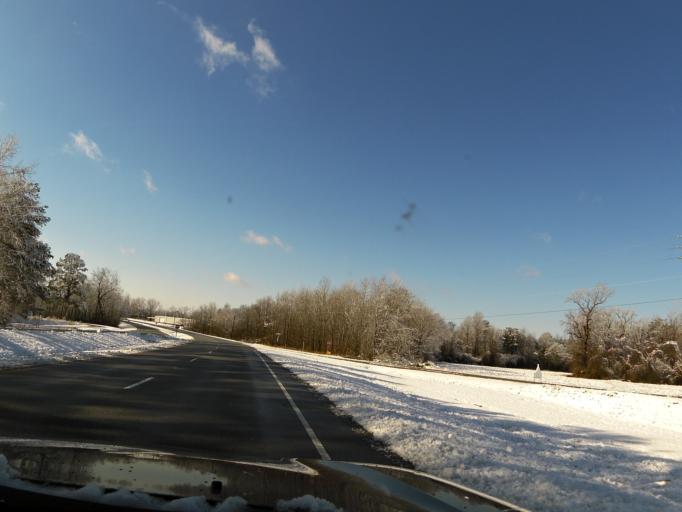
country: US
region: North Carolina
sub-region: Nash County
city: Sharpsburg
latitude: 35.8465
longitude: -77.8508
